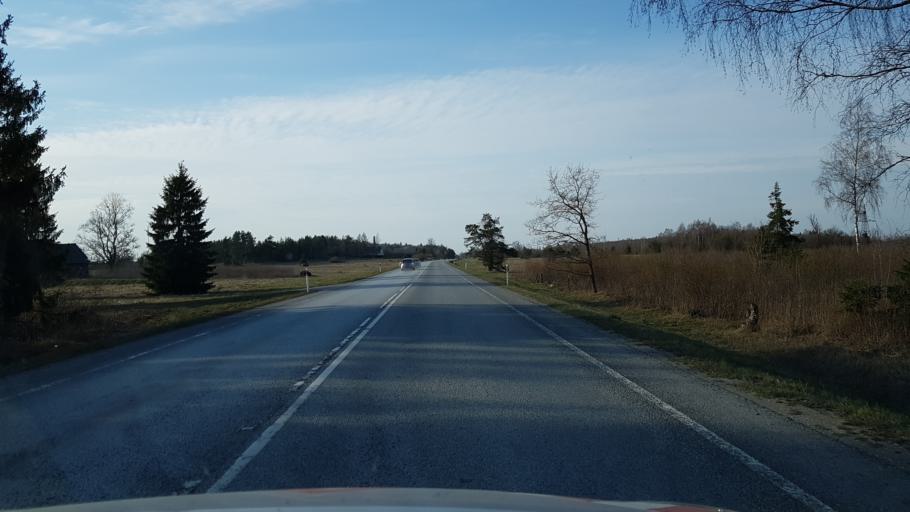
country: EE
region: Laeaene-Virumaa
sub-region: Rakvere linn
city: Rakvere
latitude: 59.3881
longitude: 26.3147
